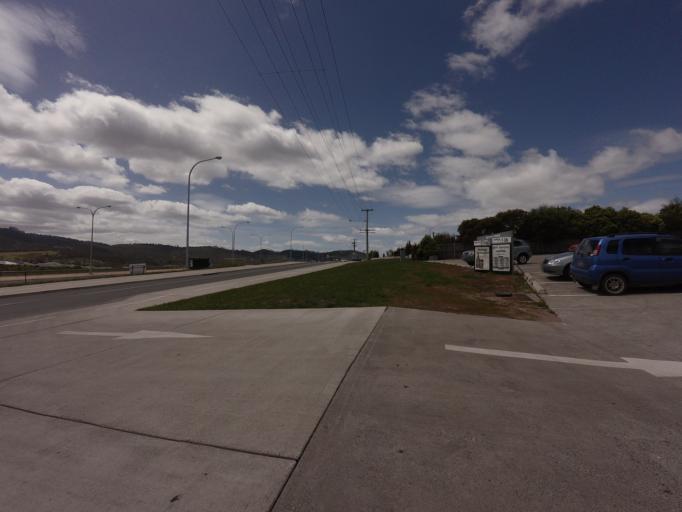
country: AU
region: Tasmania
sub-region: Clarence
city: Howrah
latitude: -42.8886
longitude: 147.4230
